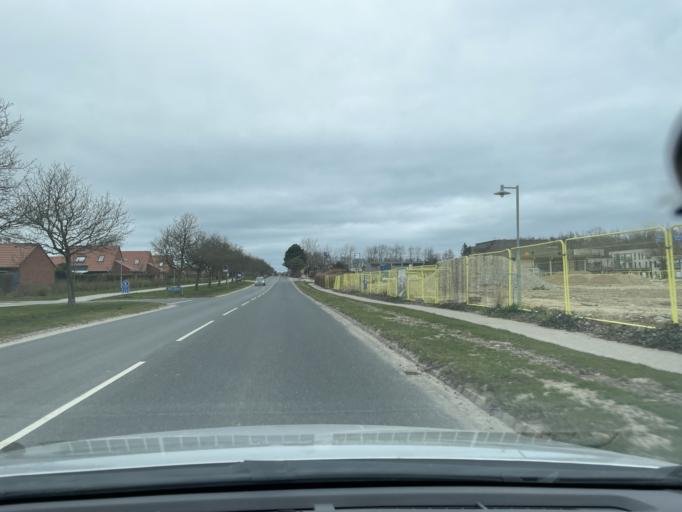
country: DK
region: South Denmark
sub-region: Nyborg Kommune
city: Nyborg
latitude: 55.3438
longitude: 10.7955
